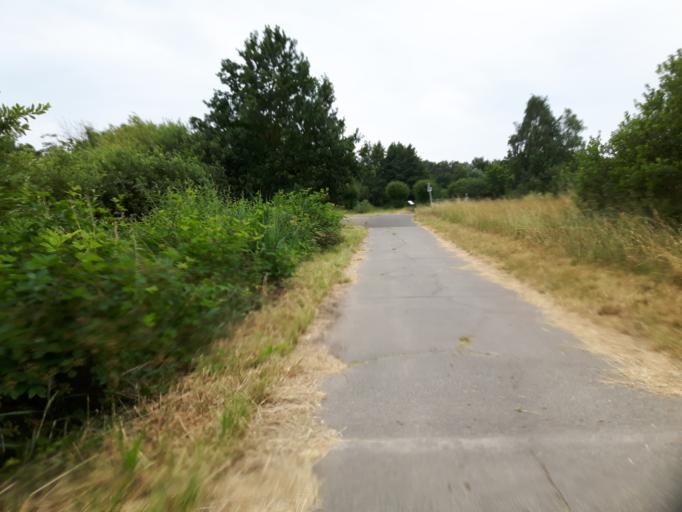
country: DE
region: Lower Saxony
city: Stelle
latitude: 53.4070
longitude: 10.0752
